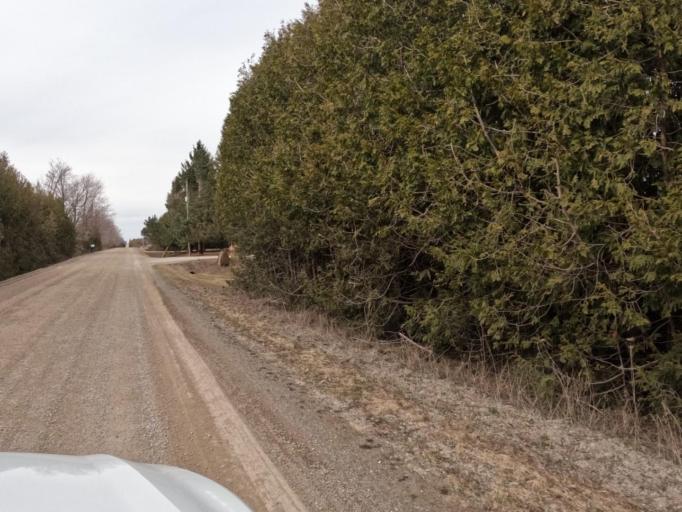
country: CA
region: Ontario
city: Shelburne
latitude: 43.9316
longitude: -80.2579
